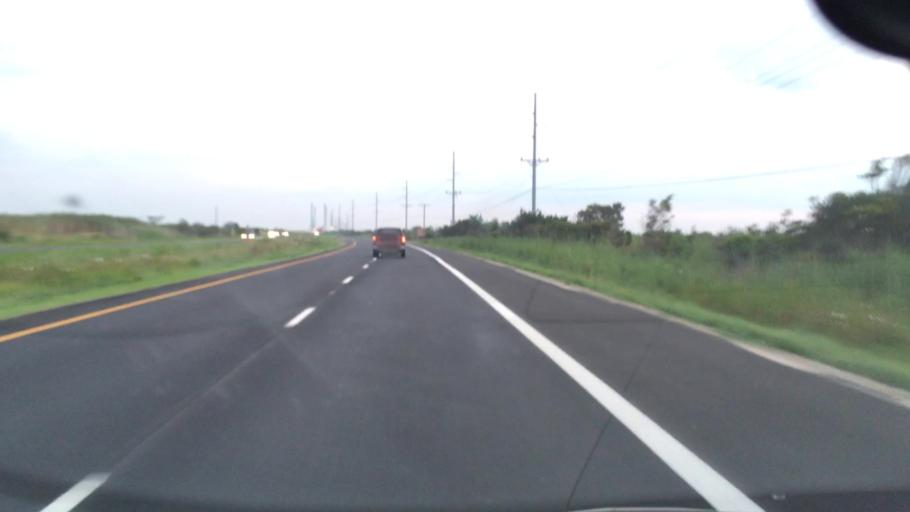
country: US
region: Delaware
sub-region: Sussex County
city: Long Neck
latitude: 38.6298
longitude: -75.0679
